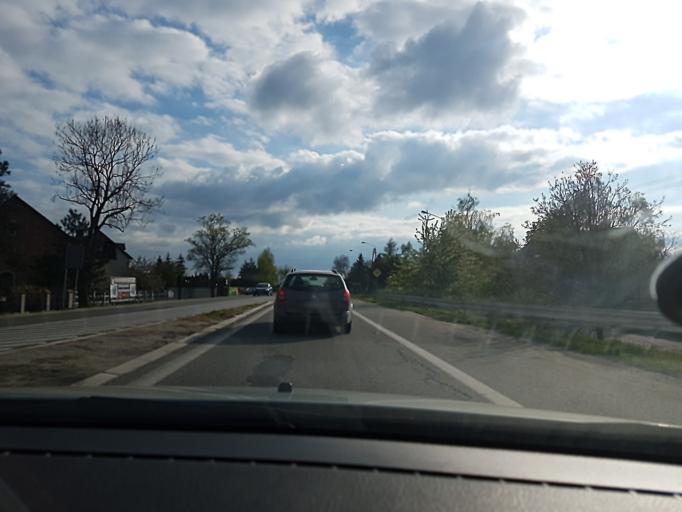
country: PL
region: Masovian Voivodeship
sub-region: Powiat sochaczewski
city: Sochaczew
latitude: 52.2305
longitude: 20.2234
